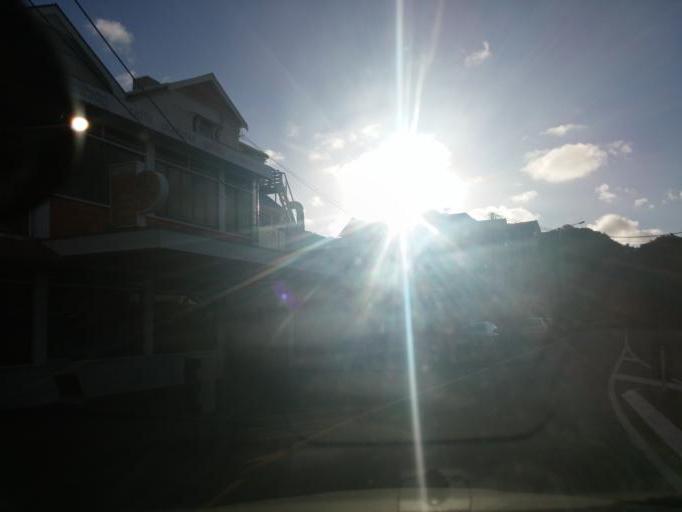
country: NZ
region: Wellington
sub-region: Wellington City
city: Kelburn
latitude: -41.2893
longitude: 174.7623
